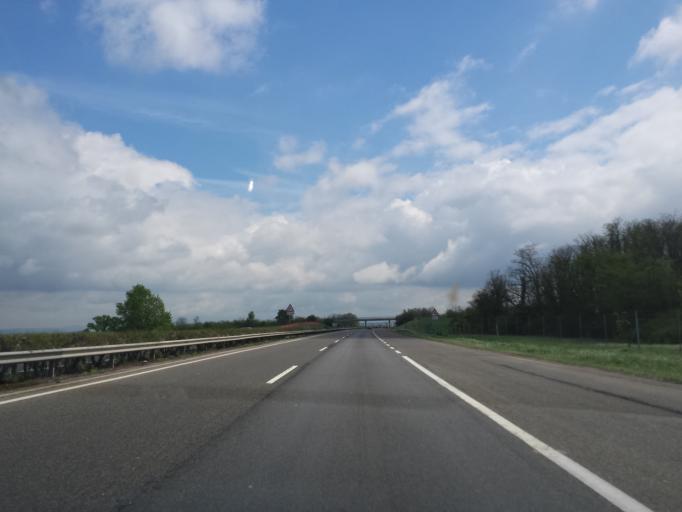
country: HU
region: Komarom-Esztergom
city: Nagyigmand
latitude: 47.6730
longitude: 18.1163
